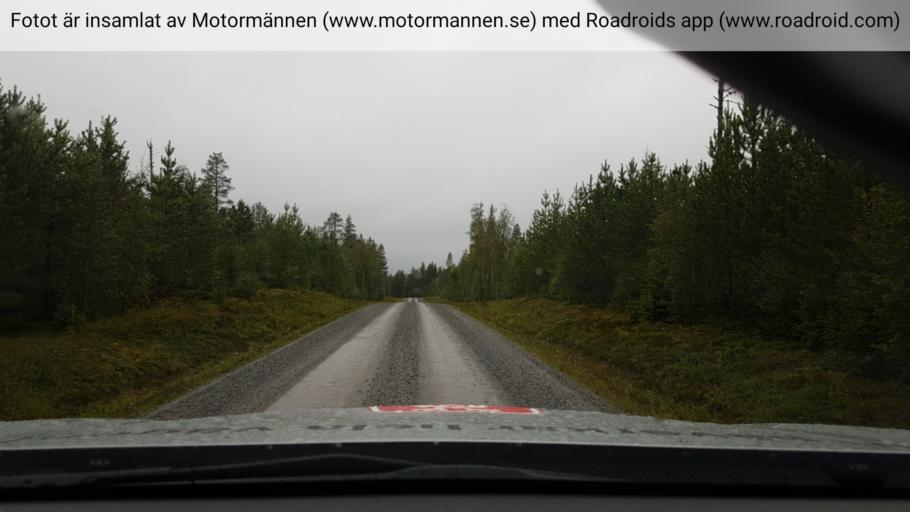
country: SE
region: Vaesterbotten
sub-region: Asele Kommun
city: Asele
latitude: 64.0154
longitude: 17.6349
